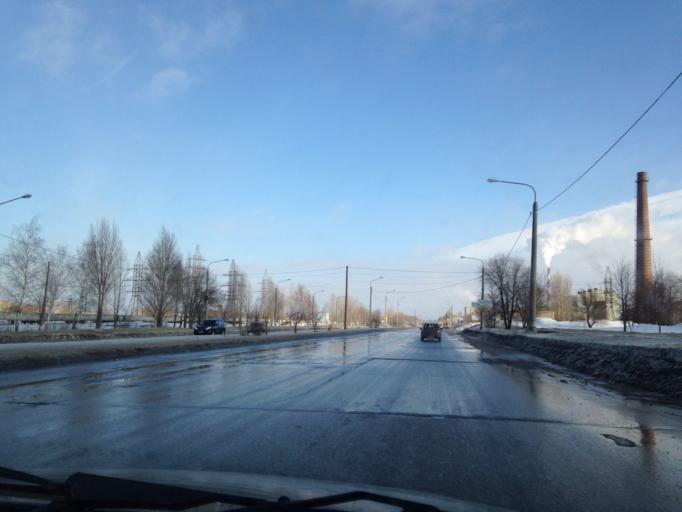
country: RU
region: Ulyanovsk
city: Mirnyy
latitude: 54.3480
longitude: 48.5772
